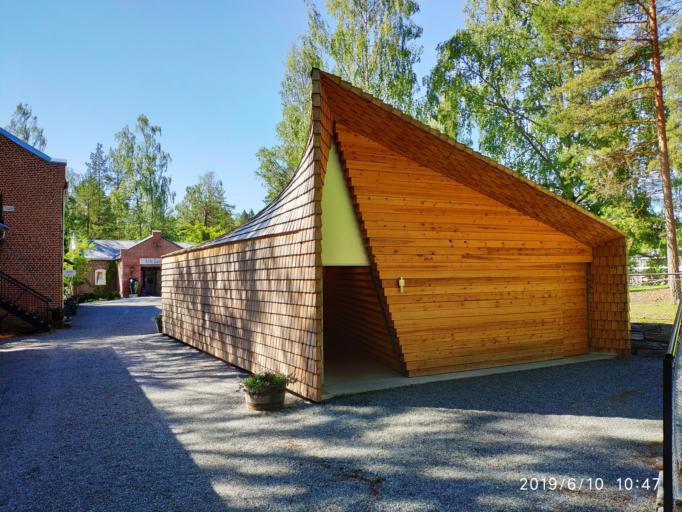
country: NO
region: Oppland
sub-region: Jevnaker
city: Jevnaker
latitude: 60.2229
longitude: 10.3705
